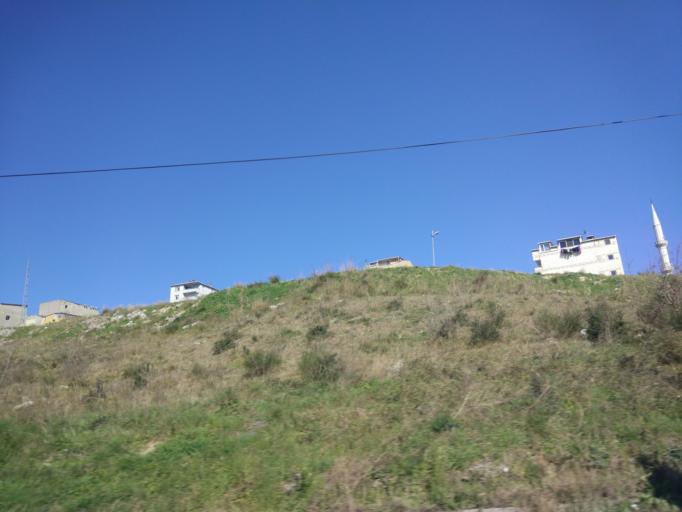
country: TR
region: Istanbul
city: Basaksehir
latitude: 41.0558
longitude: 28.7496
